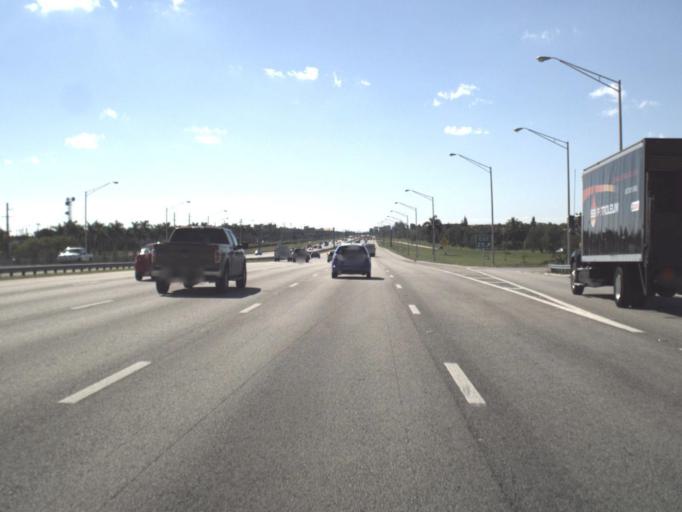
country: US
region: Florida
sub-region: Miami-Dade County
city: Sweetwater
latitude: 25.7601
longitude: -80.3855
